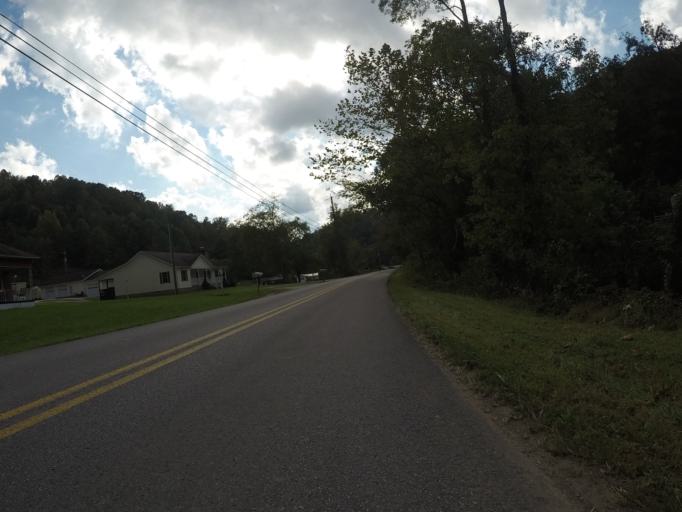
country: US
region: West Virginia
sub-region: Wayne County
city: Lavalette
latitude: 38.3525
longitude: -82.4378
